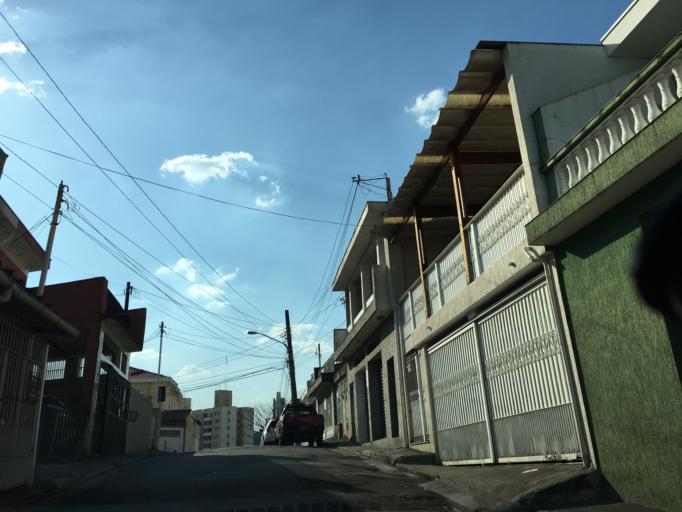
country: BR
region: Sao Paulo
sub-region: Sao Paulo
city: Sao Paulo
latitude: -23.4729
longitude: -46.6324
